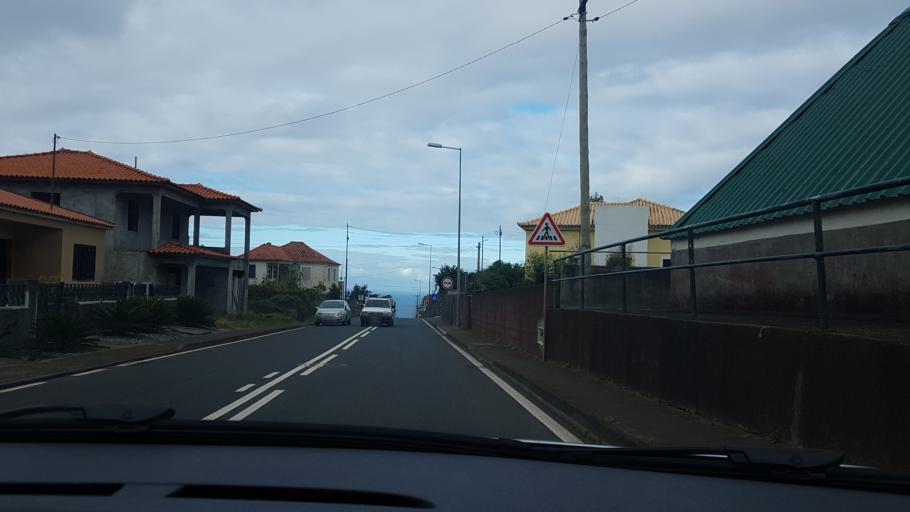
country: PT
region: Madeira
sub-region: Santana
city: Santana
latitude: 32.8173
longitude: -16.8870
